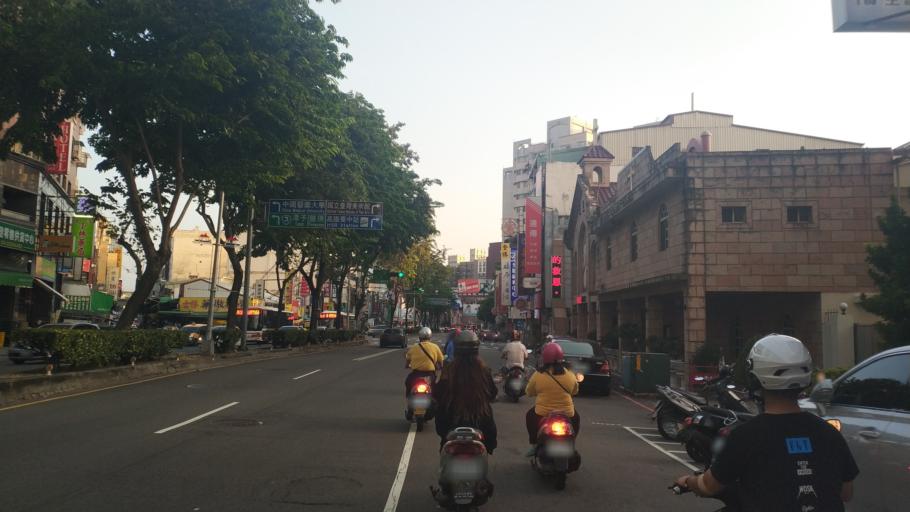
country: TW
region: Taiwan
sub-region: Taichung City
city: Taichung
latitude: 24.1534
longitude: 120.6773
